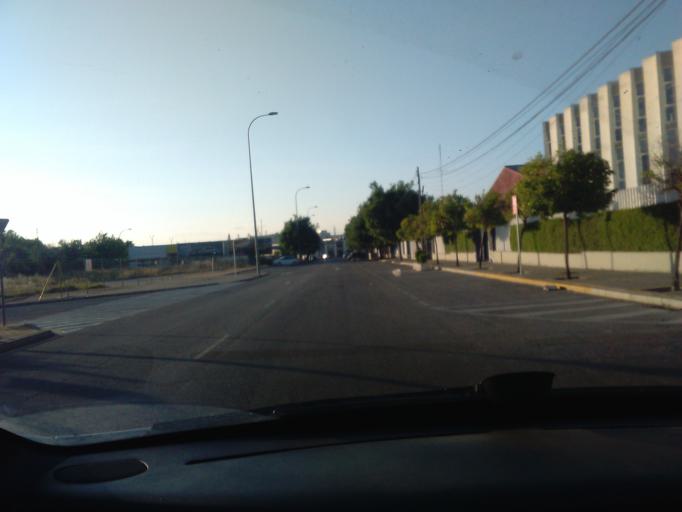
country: ES
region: Andalusia
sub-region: Provincia de Sevilla
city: Sevilla
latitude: 37.3930
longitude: -5.9462
